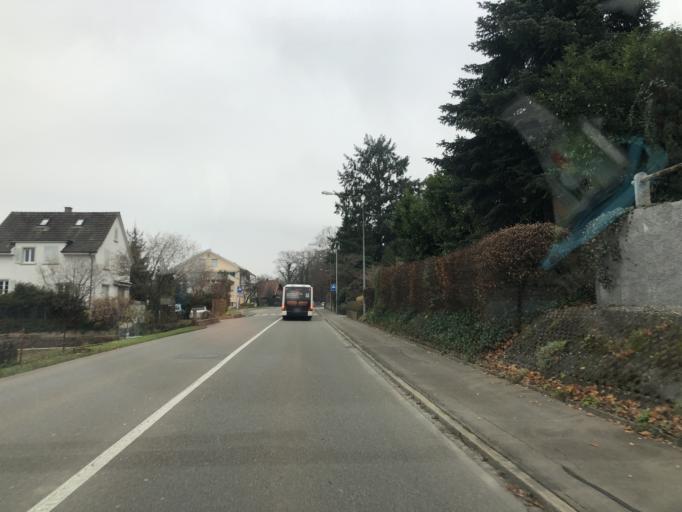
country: CH
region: Aargau
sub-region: Bezirk Baden
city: Turgi
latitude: 47.4899
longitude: 8.2498
